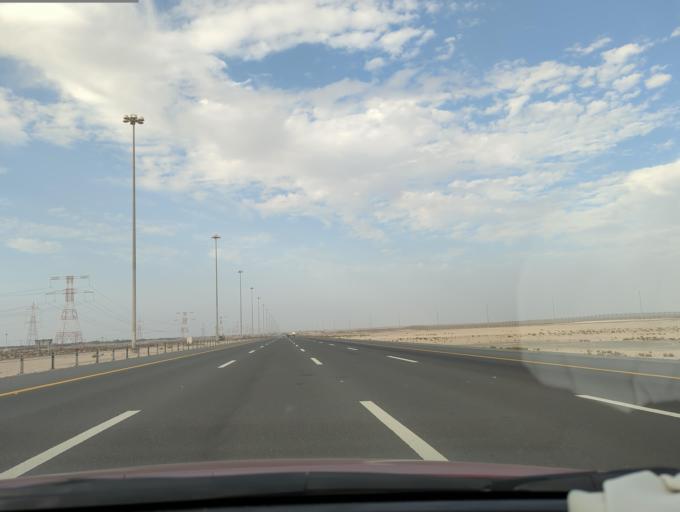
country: AE
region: Abu Dhabi
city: Abu Dhabi
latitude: 24.4740
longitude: 54.7500
